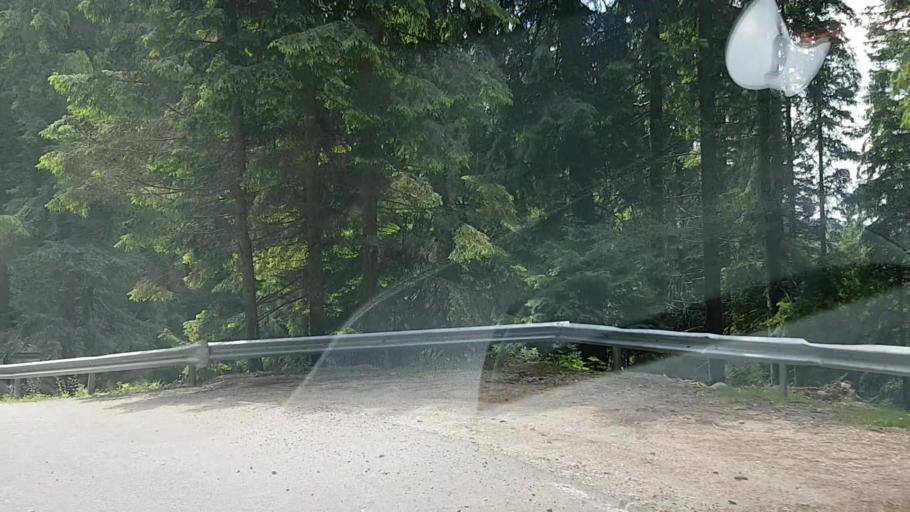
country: RO
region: Suceava
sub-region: Municipiul Campulung Moldovenesc
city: Campulung Moldovenesc
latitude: 47.4453
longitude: 25.5563
